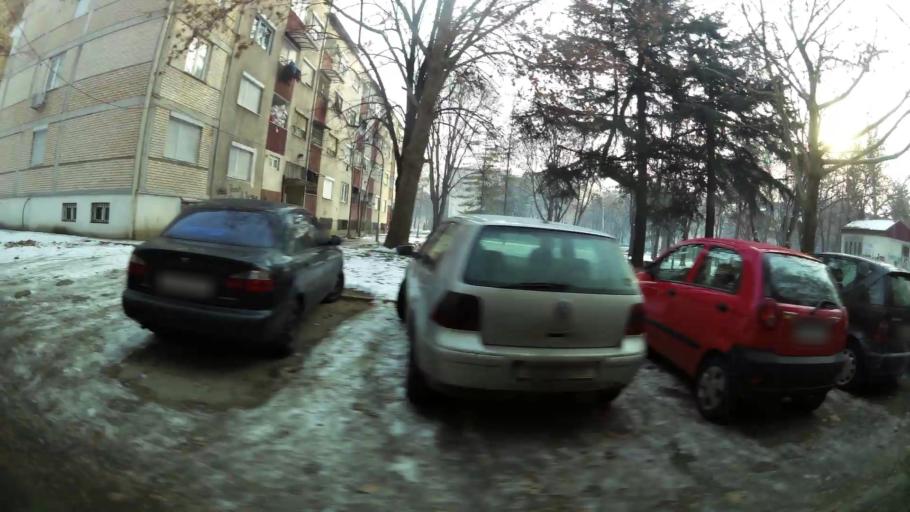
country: MK
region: Cair
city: Cair
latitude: 42.0198
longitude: 21.4424
